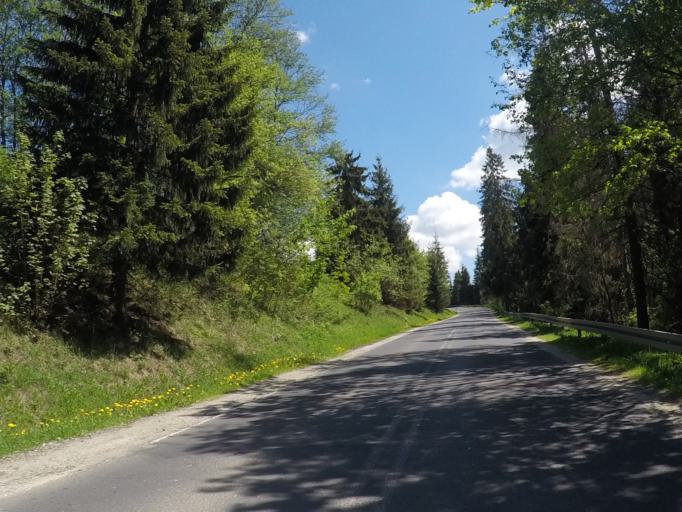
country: PL
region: Lesser Poland Voivodeship
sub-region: Powiat tatrzanski
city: Bukowina Tatrzanska
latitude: 49.3335
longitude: 20.0799
